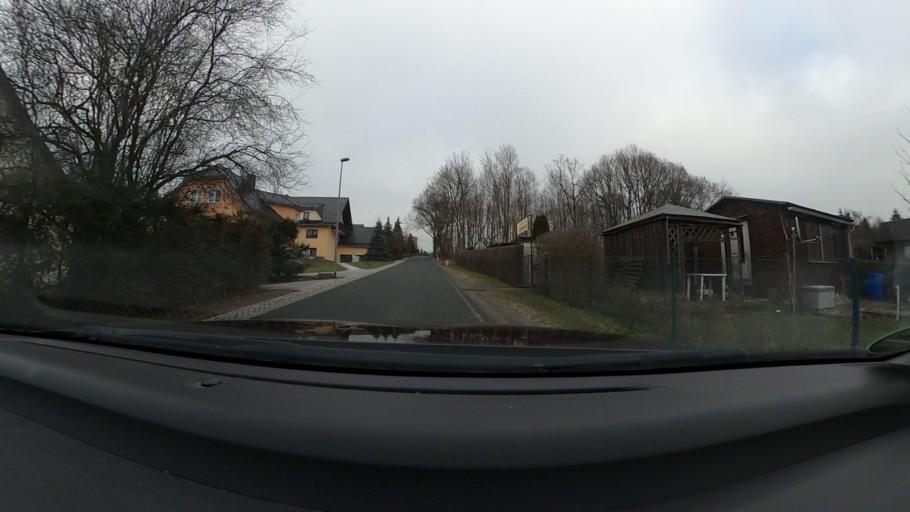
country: DE
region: Saxony
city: Oberschona
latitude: 50.9072
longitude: 13.2959
